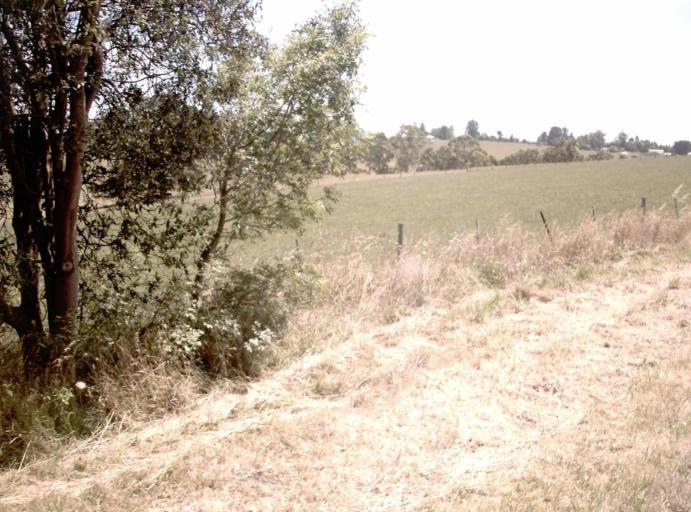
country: AU
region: Victoria
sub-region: Baw Baw
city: Warragul
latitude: -38.2415
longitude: 145.9140
